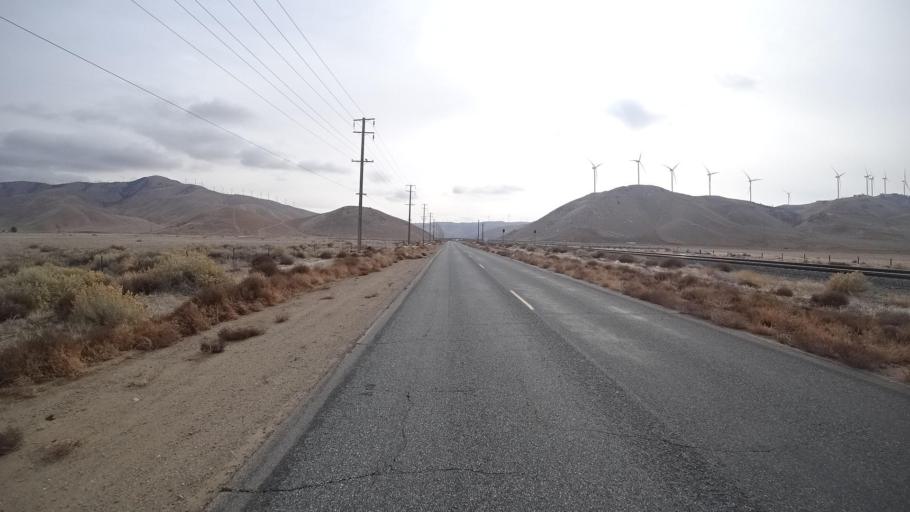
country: US
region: California
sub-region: Kern County
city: Tehachapi
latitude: 35.1171
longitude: -118.3370
